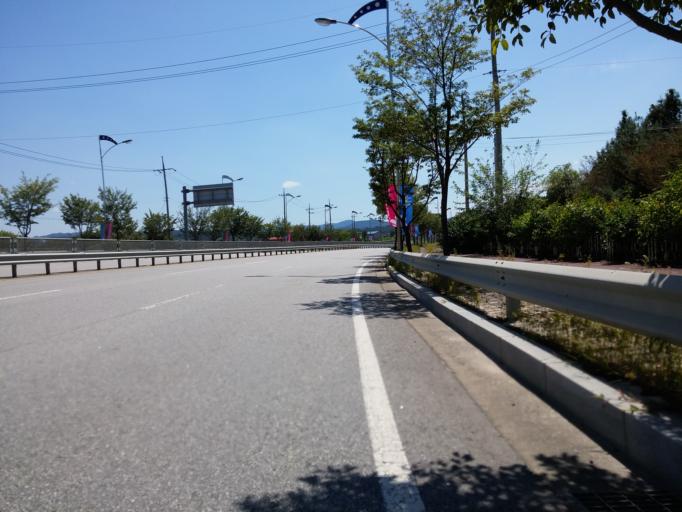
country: KR
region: Chungcheongbuk-do
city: Cheongju-si
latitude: 36.6286
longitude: 127.3358
